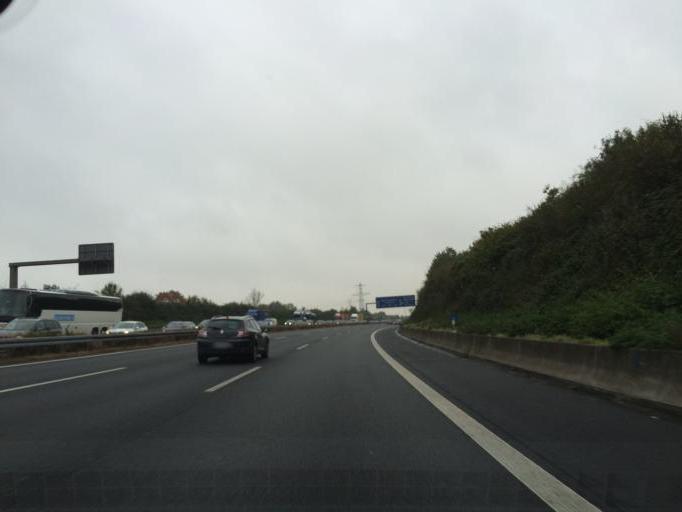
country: DE
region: North Rhine-Westphalia
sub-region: Regierungsbezirk Dusseldorf
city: Oberhausen
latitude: 51.5043
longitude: 6.8227
